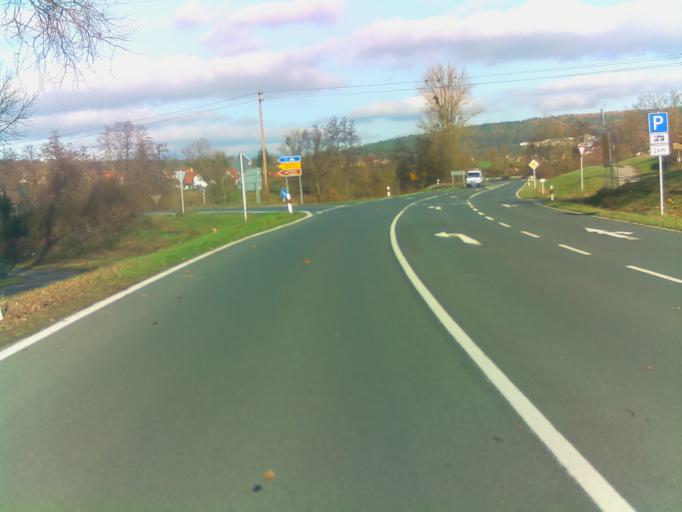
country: DE
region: Bavaria
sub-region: Regierungsbezirk Unterfranken
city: Bad Bocklet
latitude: 50.2524
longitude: 10.0650
